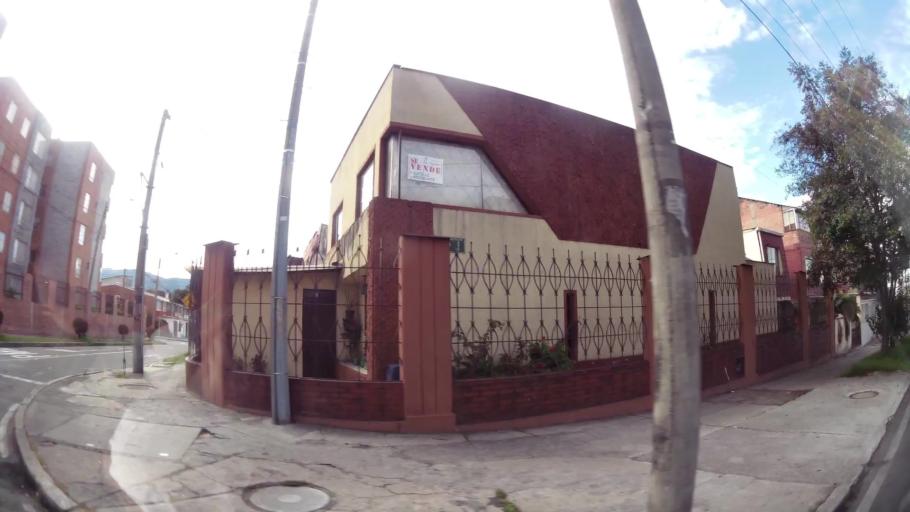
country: CO
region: Bogota D.C.
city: Barrio San Luis
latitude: 4.6918
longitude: -74.0785
